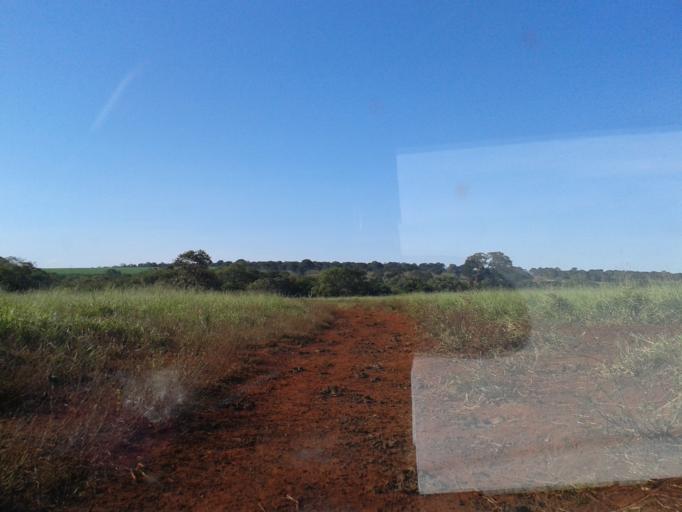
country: BR
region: Minas Gerais
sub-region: Santa Vitoria
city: Santa Vitoria
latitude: -18.9939
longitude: -50.3510
